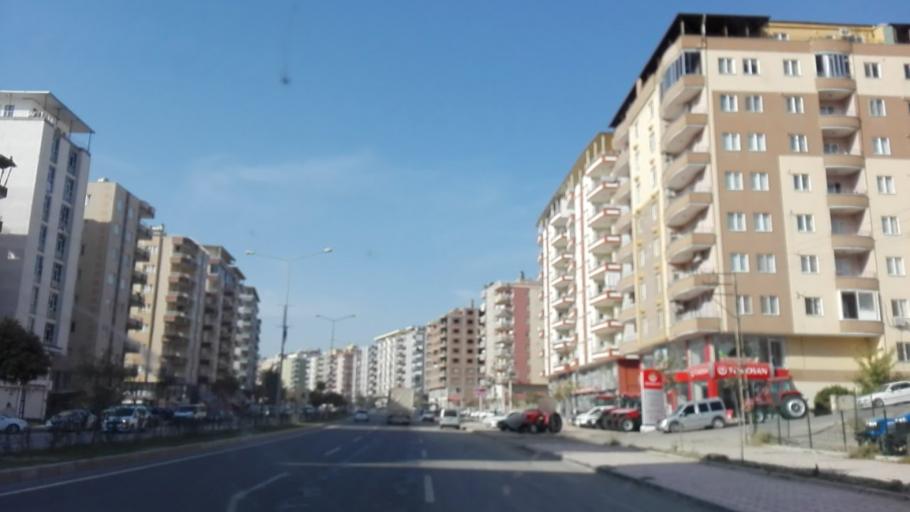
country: TR
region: Batman
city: Aydinkonak
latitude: 37.8985
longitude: 41.1471
